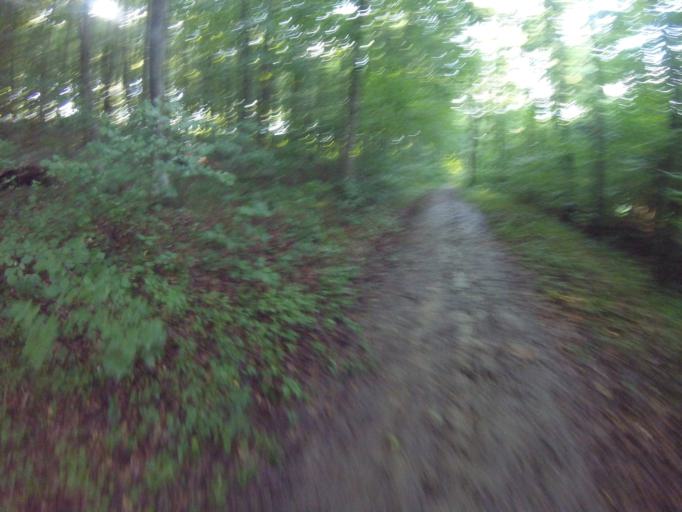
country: HU
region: Zala
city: Becsehely
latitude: 46.4989
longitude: 16.7384
